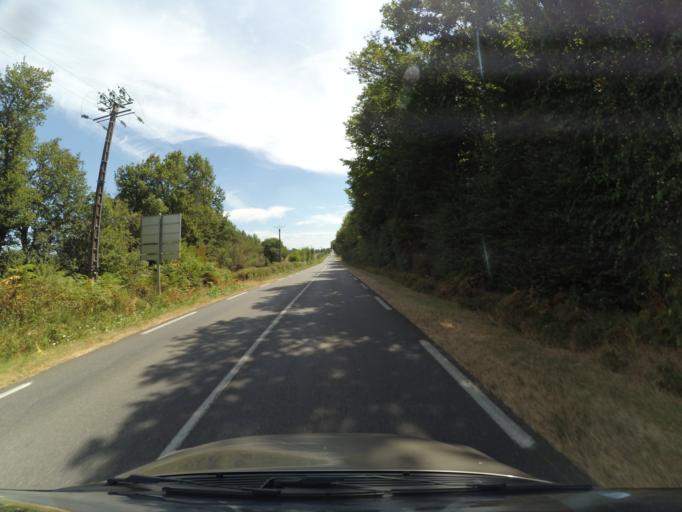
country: FR
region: Poitou-Charentes
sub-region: Departement de la Vienne
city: Availles-Limouzine
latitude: 46.0932
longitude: 0.5841
